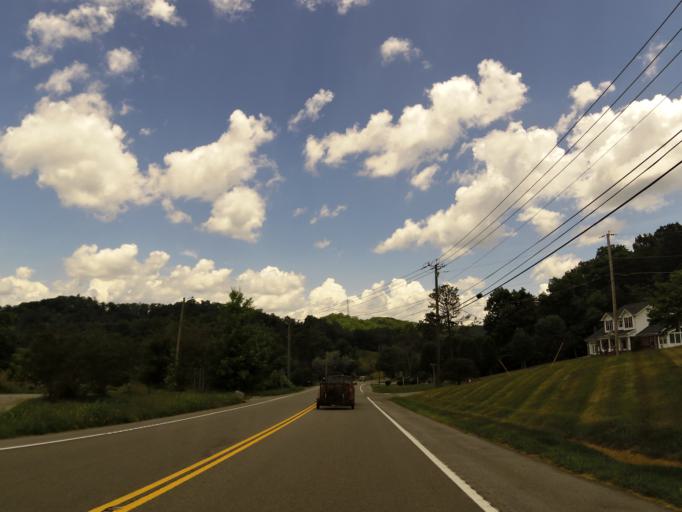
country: US
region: Tennessee
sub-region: Union County
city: Maynardville
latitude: 36.2832
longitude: -83.7617
